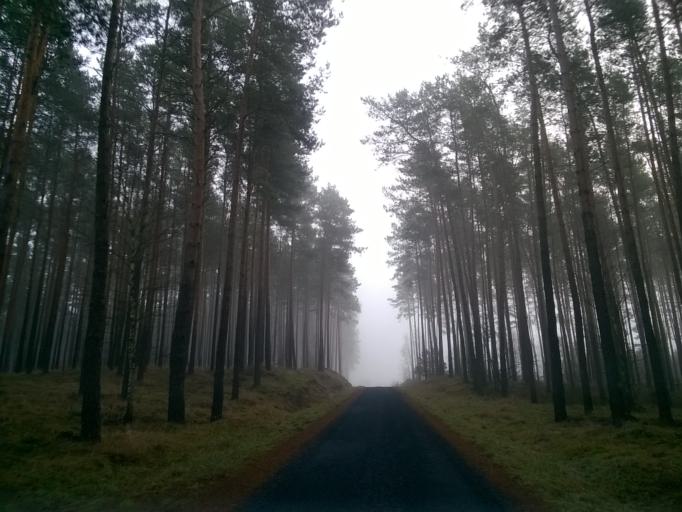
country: PL
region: Kujawsko-Pomorskie
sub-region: Powiat nakielski
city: Kcynia
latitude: 53.0529
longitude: 17.4541
